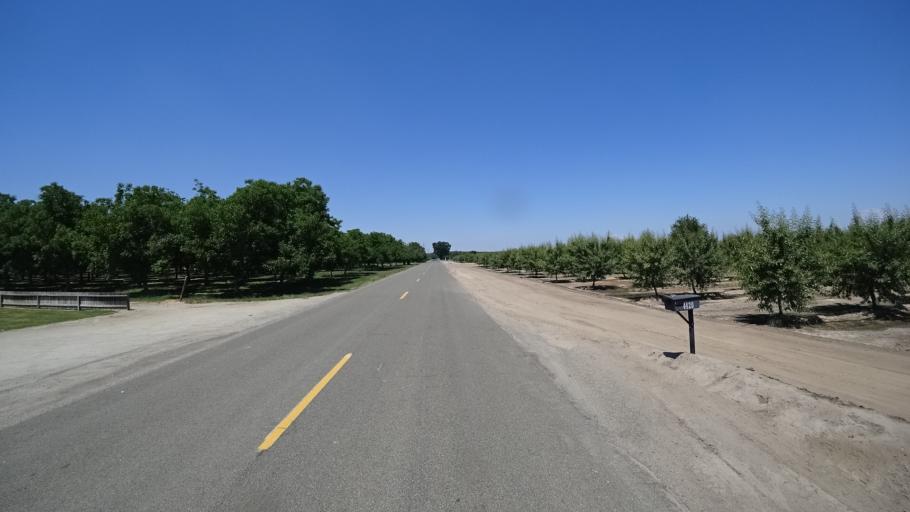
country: US
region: California
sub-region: Kings County
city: Lucerne
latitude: 36.4101
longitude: -119.6549
